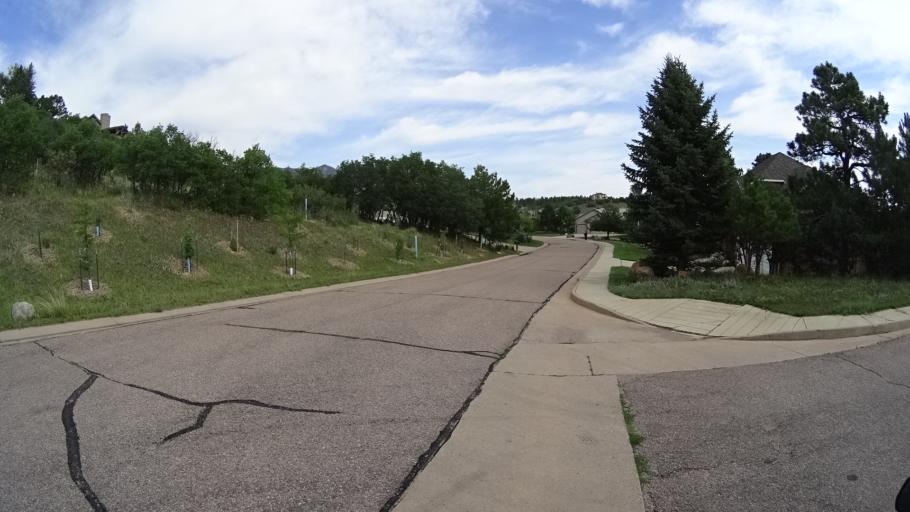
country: US
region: Colorado
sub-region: El Paso County
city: Air Force Academy
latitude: 38.9484
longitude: -104.8598
